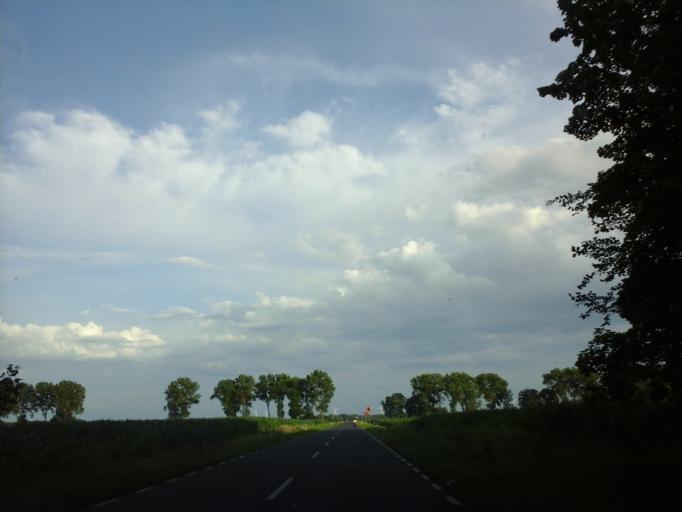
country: PL
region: West Pomeranian Voivodeship
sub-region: Powiat kamienski
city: Kamien Pomorski
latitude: 53.9161
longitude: 14.8472
